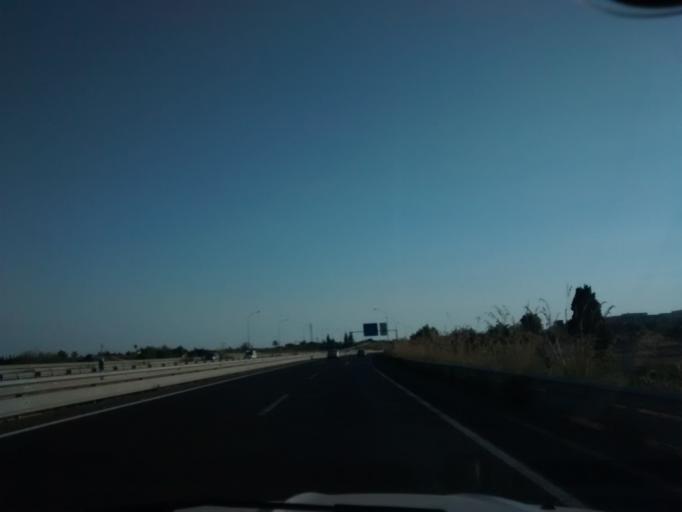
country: ES
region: Balearic Islands
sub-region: Illes Balears
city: Inca
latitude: 39.7187
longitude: 2.9267
